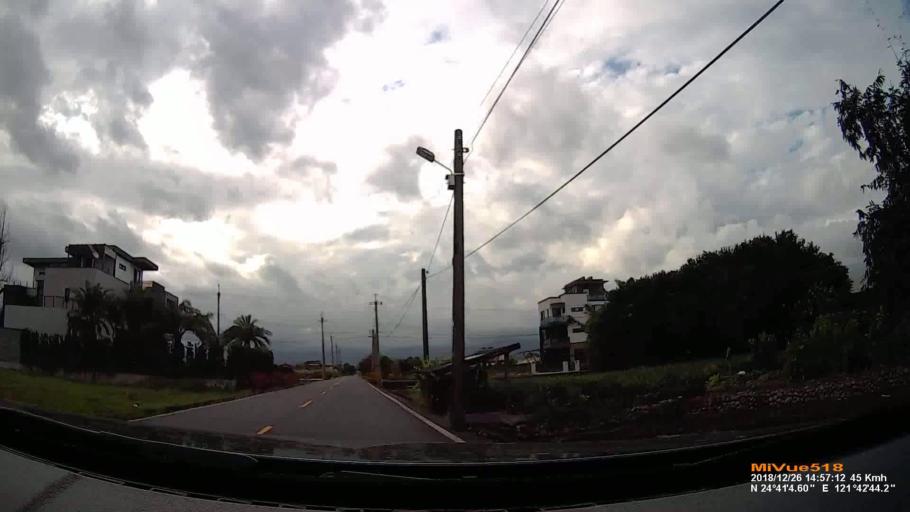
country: TW
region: Taiwan
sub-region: Yilan
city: Yilan
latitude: 24.6846
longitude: 121.7121
